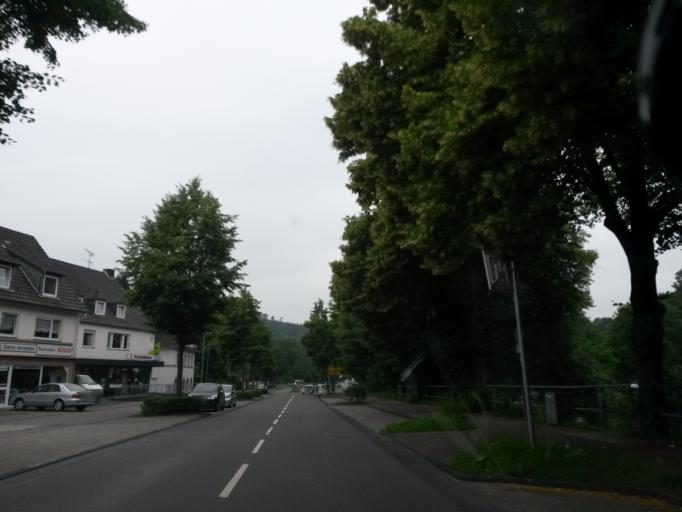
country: DE
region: North Rhine-Westphalia
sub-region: Regierungsbezirk Koln
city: Engelskirchen
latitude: 50.9753
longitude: 7.3670
